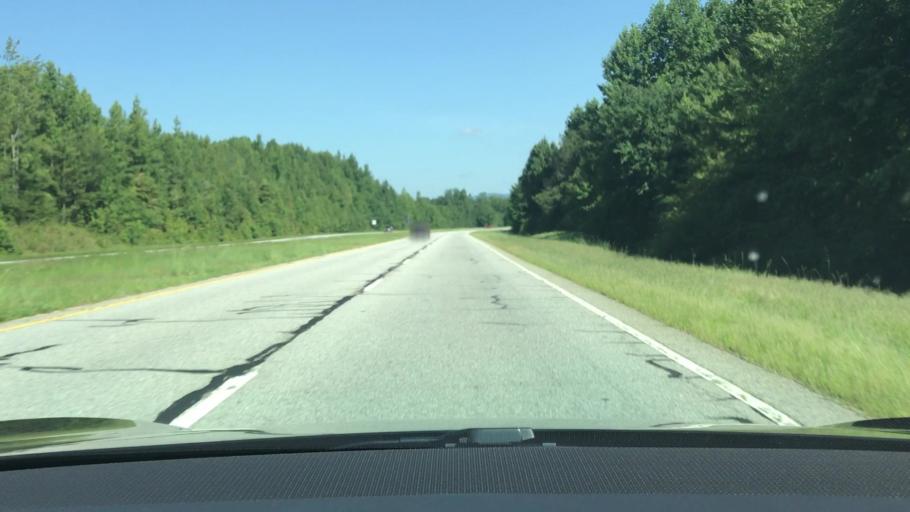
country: US
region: Georgia
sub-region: Habersham County
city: Clarkesville
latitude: 34.6048
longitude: -83.4470
